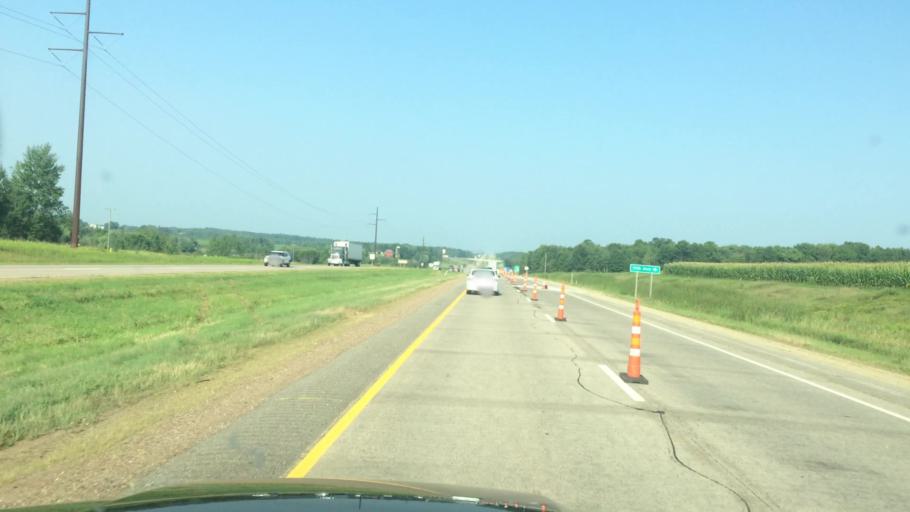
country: US
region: Wisconsin
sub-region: Marathon County
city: Edgar
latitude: 44.9446
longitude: -89.9413
